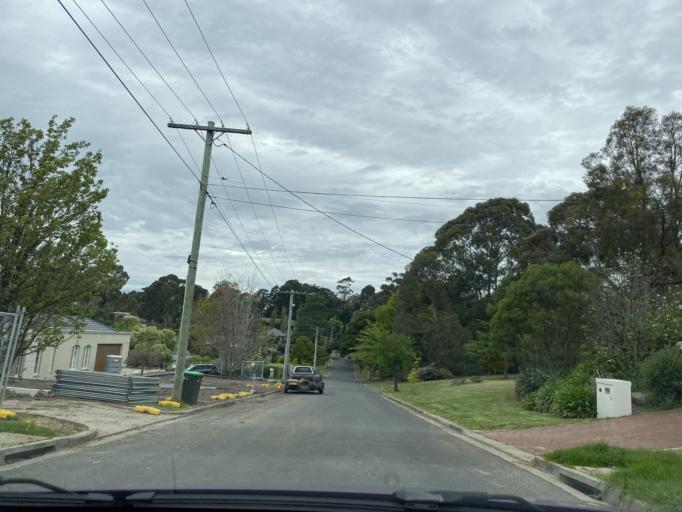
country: AU
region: Victoria
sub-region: Manningham
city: Templestowe Lower
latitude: -37.7613
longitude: 145.1353
